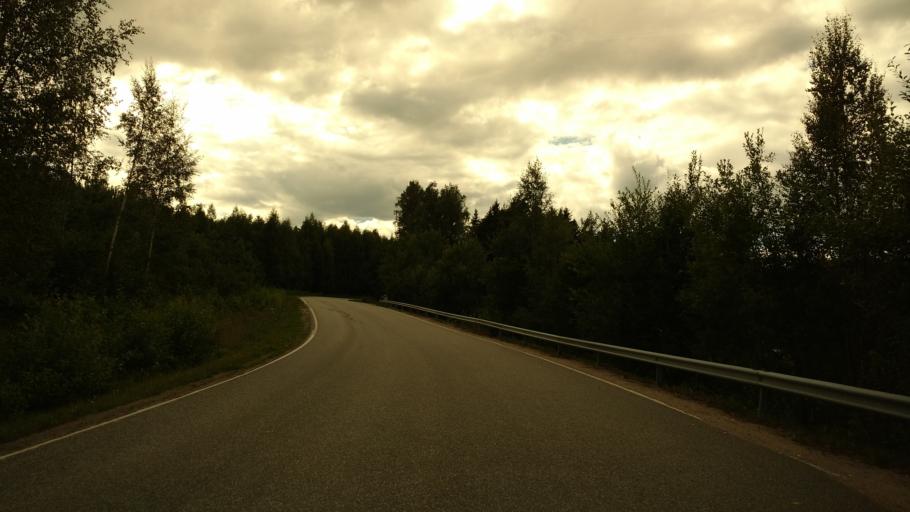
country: FI
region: Varsinais-Suomi
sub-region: Salo
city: Halikko
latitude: 60.4020
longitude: 23.0100
